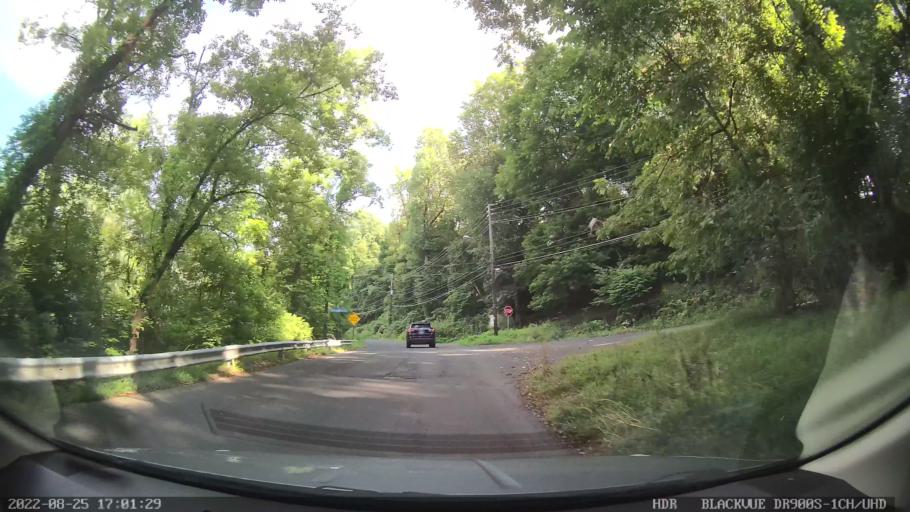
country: US
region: Pennsylvania
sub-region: Lehigh County
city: Emmaus
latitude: 40.5565
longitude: -75.5088
